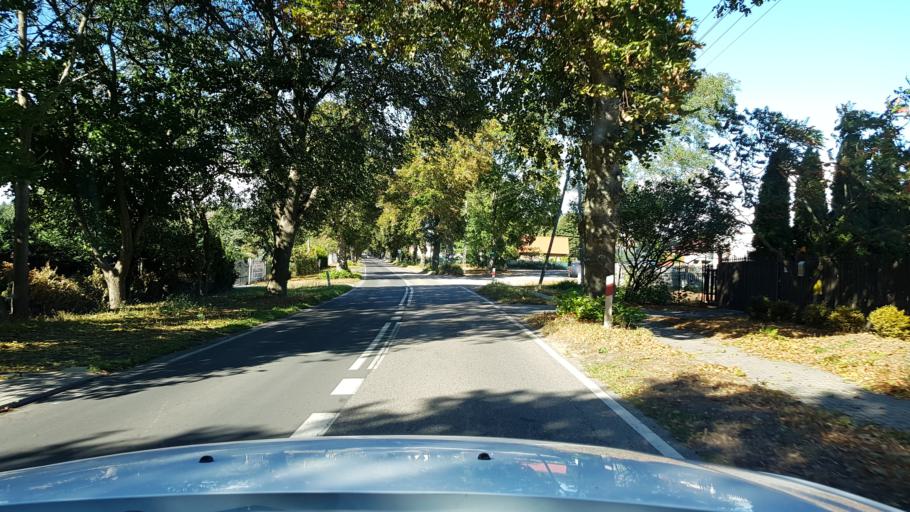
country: PL
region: West Pomeranian Voivodeship
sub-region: Powiat gryfinski
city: Gryfino
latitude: 53.2106
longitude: 14.5003
